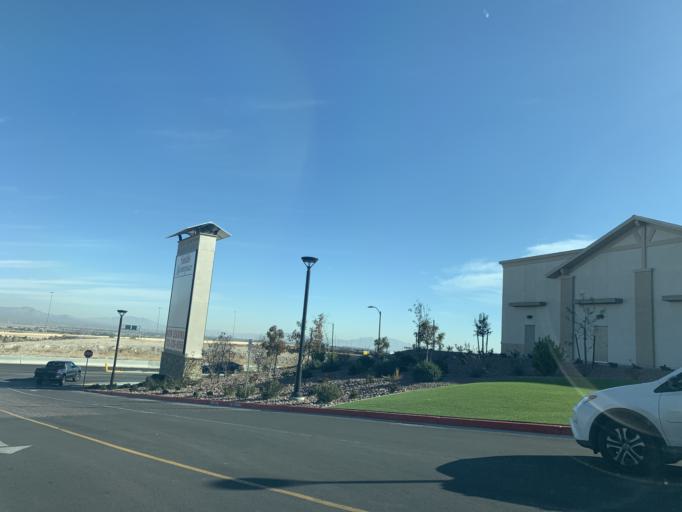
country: US
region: Nevada
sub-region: Clark County
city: Summerlin South
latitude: 36.3160
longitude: -115.3068
